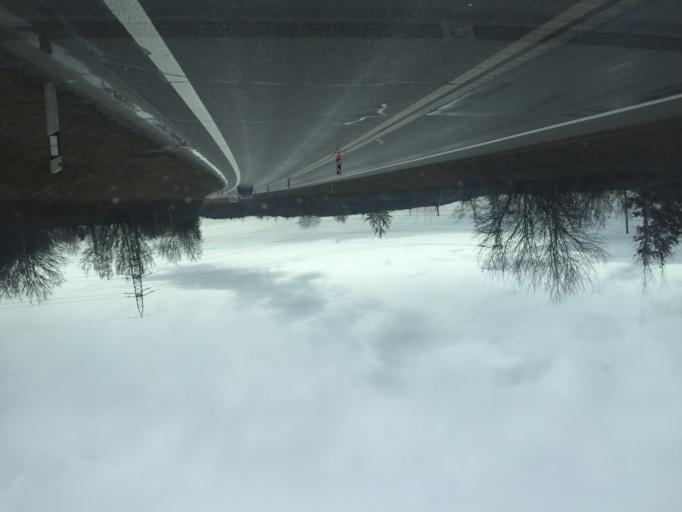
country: CH
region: Zurich
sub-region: Bezirk Winterthur
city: Hettlingen
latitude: 47.5319
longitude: 8.6938
